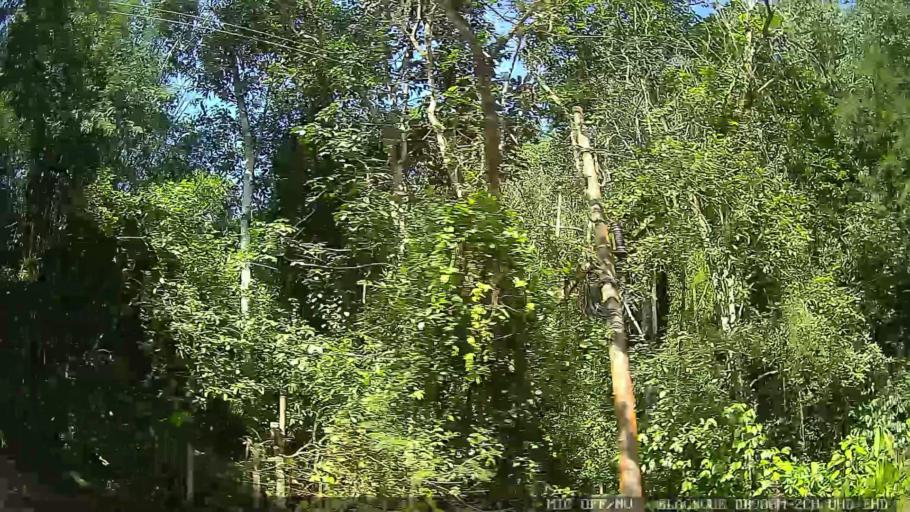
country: BR
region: Sao Paulo
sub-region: Santos
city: Santos
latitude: -24.0033
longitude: -46.3109
